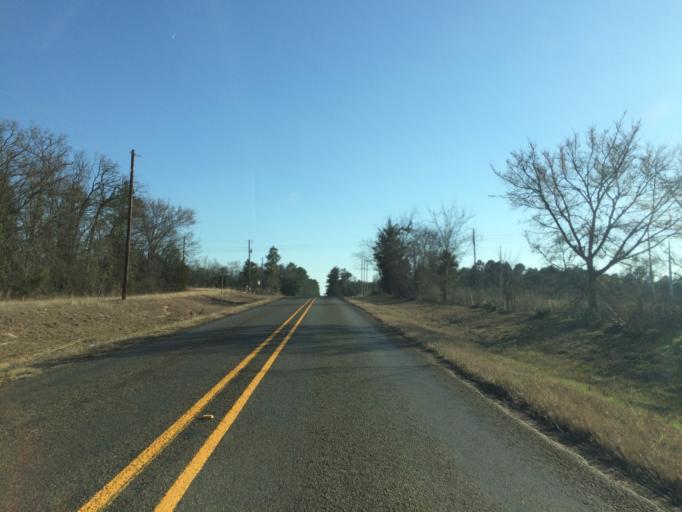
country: US
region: Texas
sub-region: Wood County
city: Hawkins
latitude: 32.6407
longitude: -95.3132
